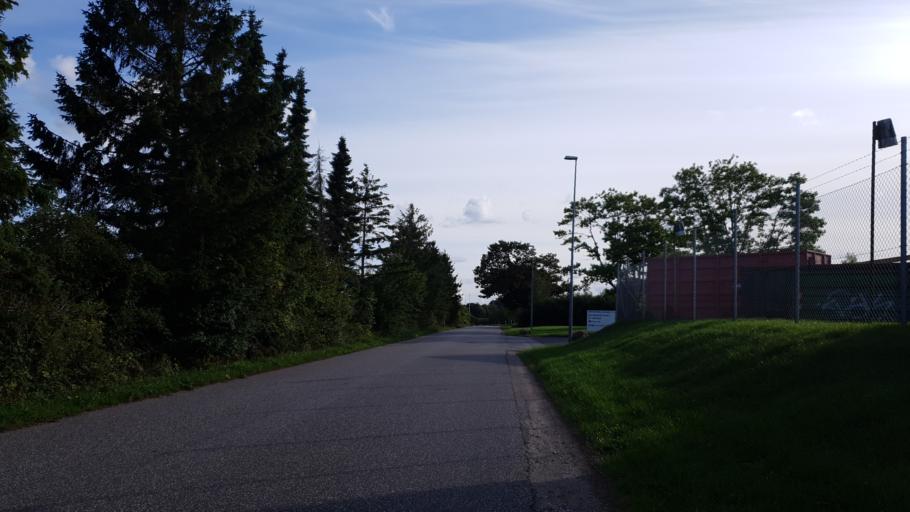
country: DK
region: South Denmark
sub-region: Fredericia Kommune
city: Snoghoj
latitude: 55.5454
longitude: 9.6900
